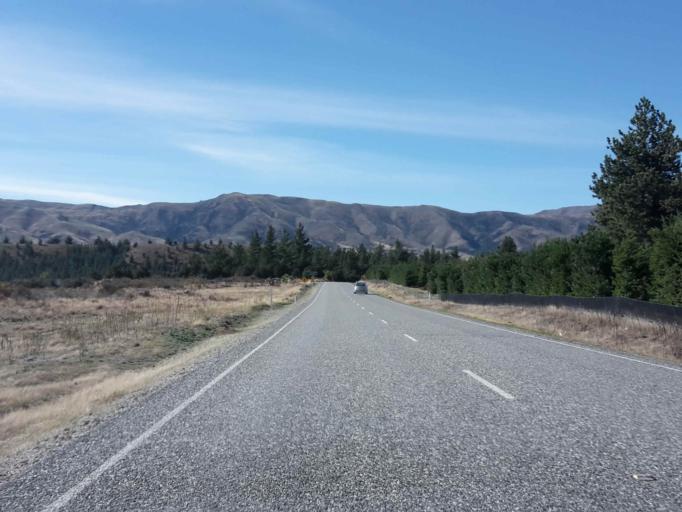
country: NZ
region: Otago
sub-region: Queenstown-Lakes District
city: Wanaka
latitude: -44.7339
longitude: 169.2733
